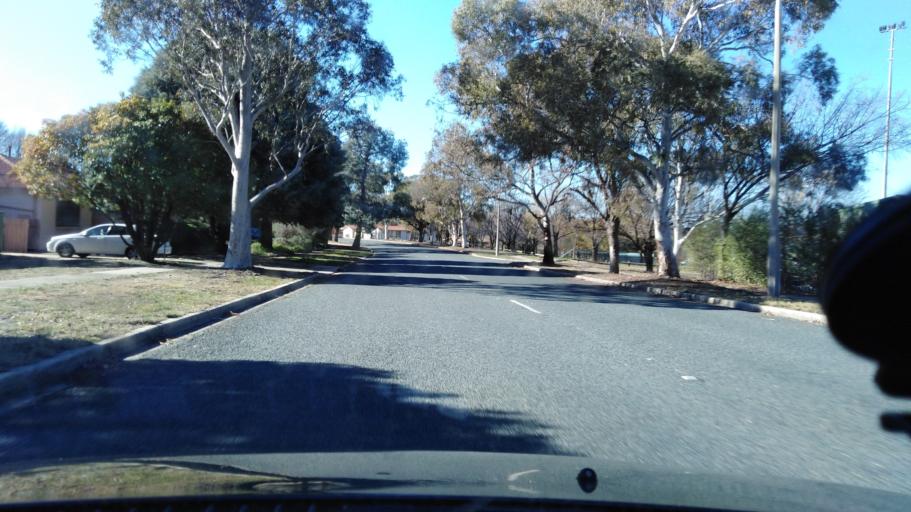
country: AU
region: Australian Capital Territory
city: Forrest
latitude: -35.3460
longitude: 149.0370
